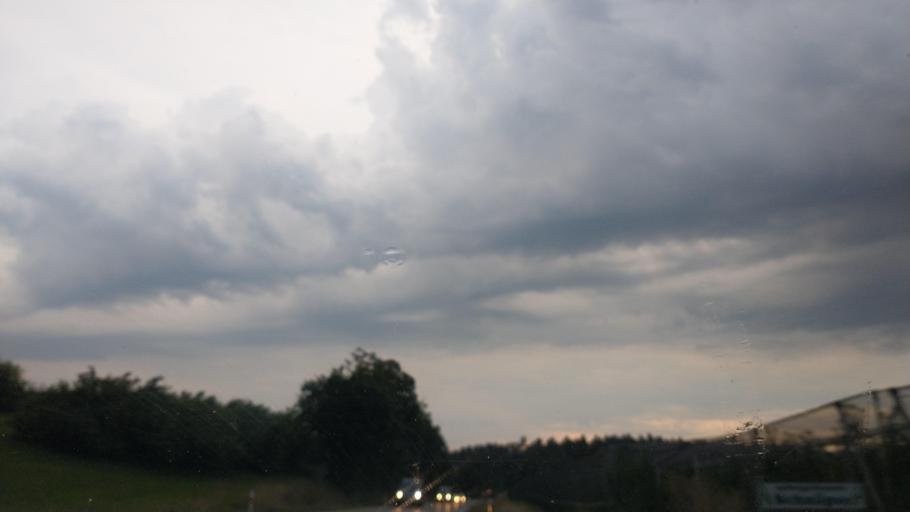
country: DE
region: Baden-Wuerttemberg
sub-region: Tuebingen Region
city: Tettnang
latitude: 47.6688
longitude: 9.6174
